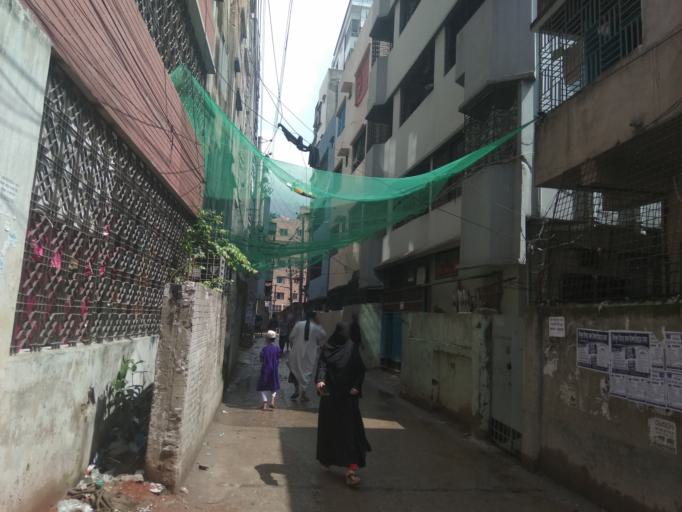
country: BD
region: Dhaka
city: Azimpur
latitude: 23.7981
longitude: 90.3810
